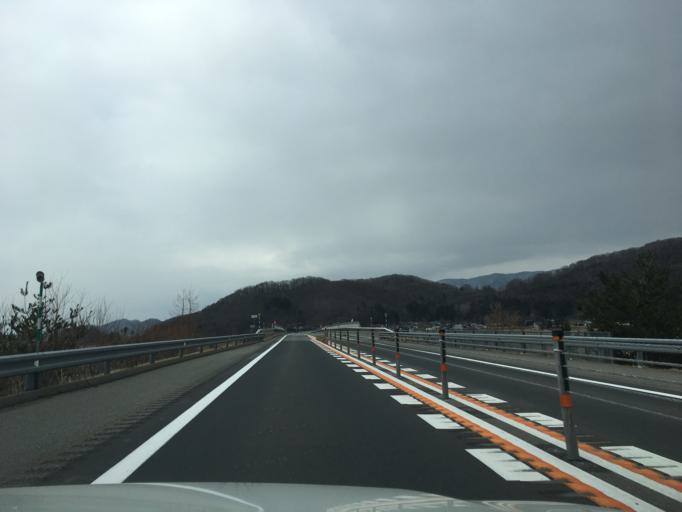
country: JP
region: Aomori
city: Aomori Shi
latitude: 40.8111
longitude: 140.8031
